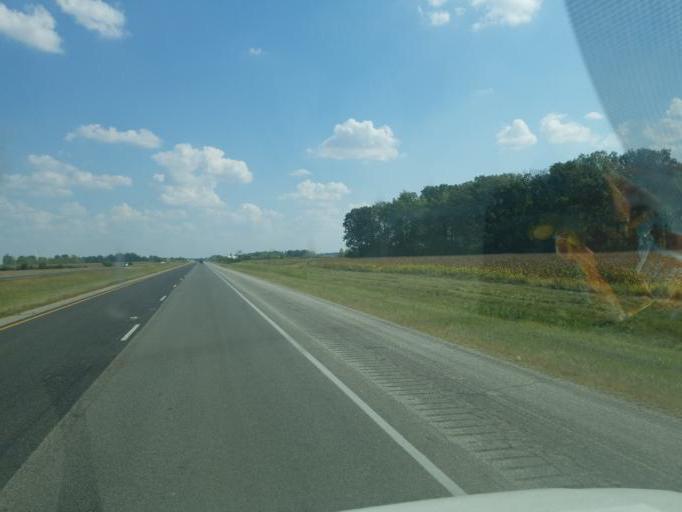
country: US
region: Indiana
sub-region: Allen County
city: Monroeville
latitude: 41.0112
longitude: -84.8558
